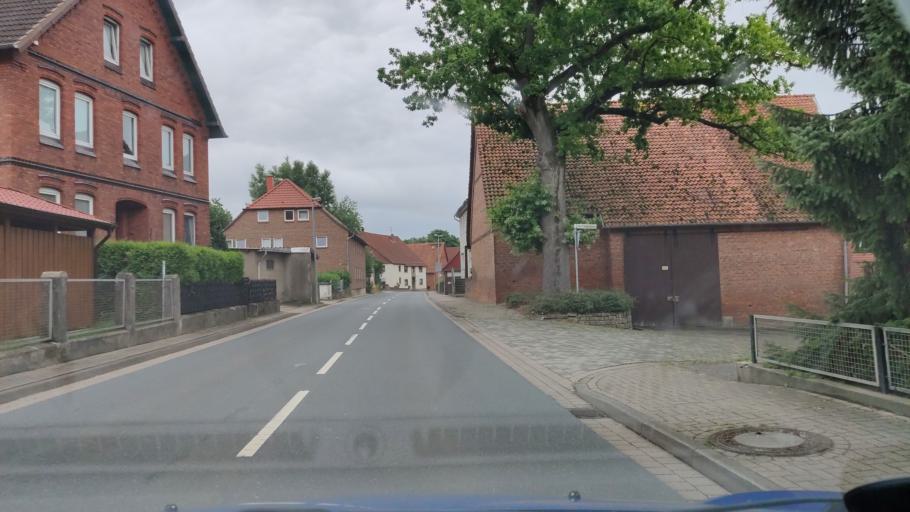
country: DE
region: Lower Saxony
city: Bad Munder am Deister
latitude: 52.1639
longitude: 9.4847
